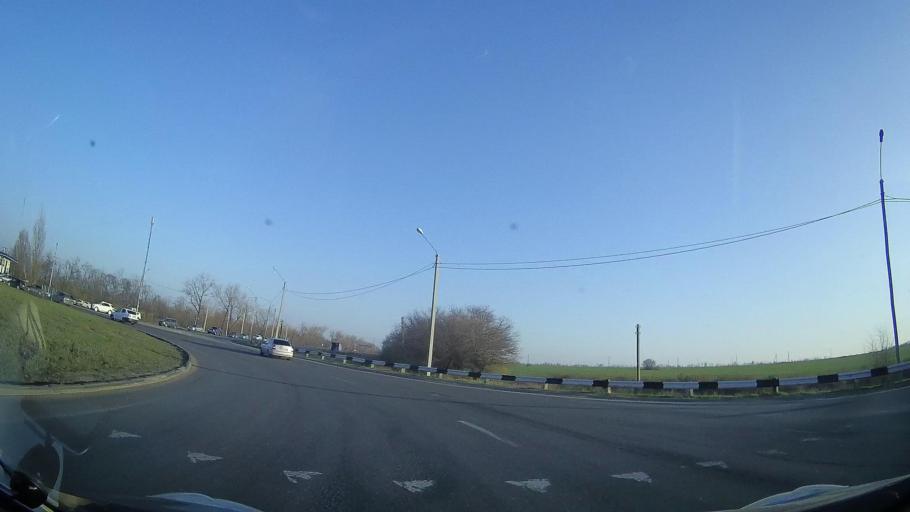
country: RU
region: Rostov
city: Bataysk
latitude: 47.0811
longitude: 39.7733
